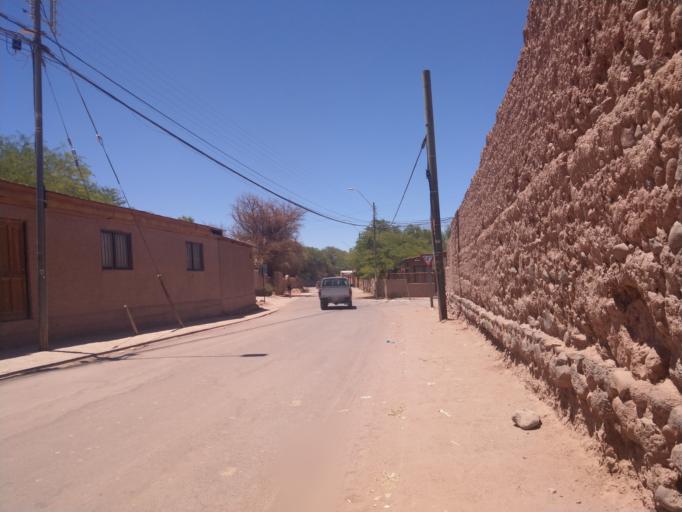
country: CL
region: Antofagasta
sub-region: Provincia de El Loa
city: San Pedro de Atacama
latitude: -22.9137
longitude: -68.2009
